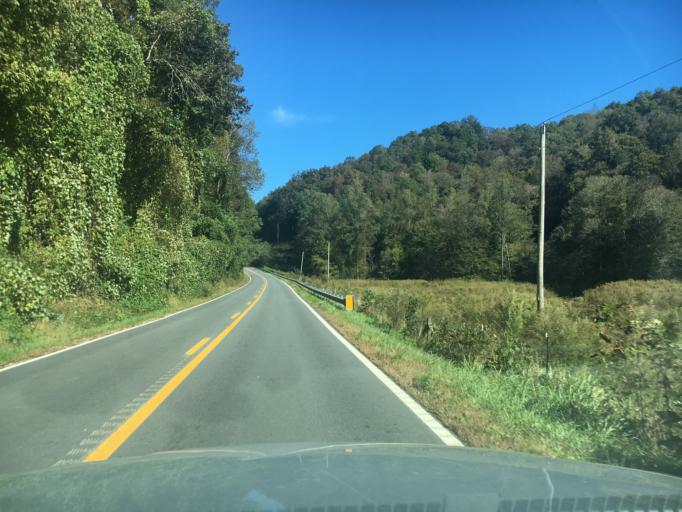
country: US
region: North Carolina
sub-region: Burke County
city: Glen Alpine
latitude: 35.5598
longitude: -81.8531
